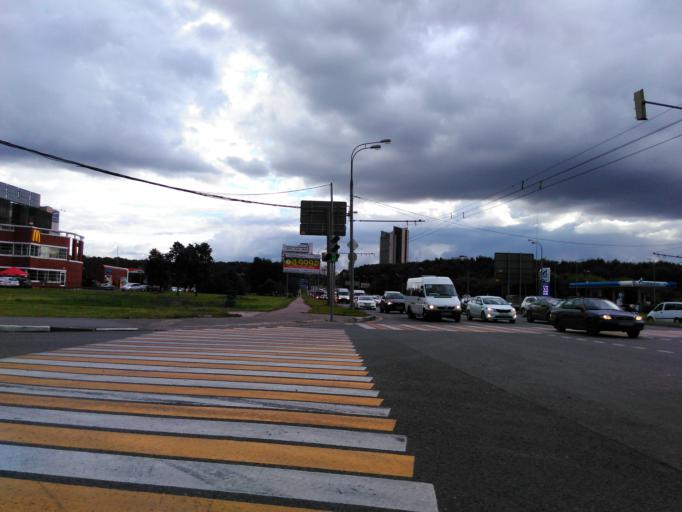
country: RU
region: Moscow
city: Troparevo
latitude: 55.6631
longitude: 37.5091
